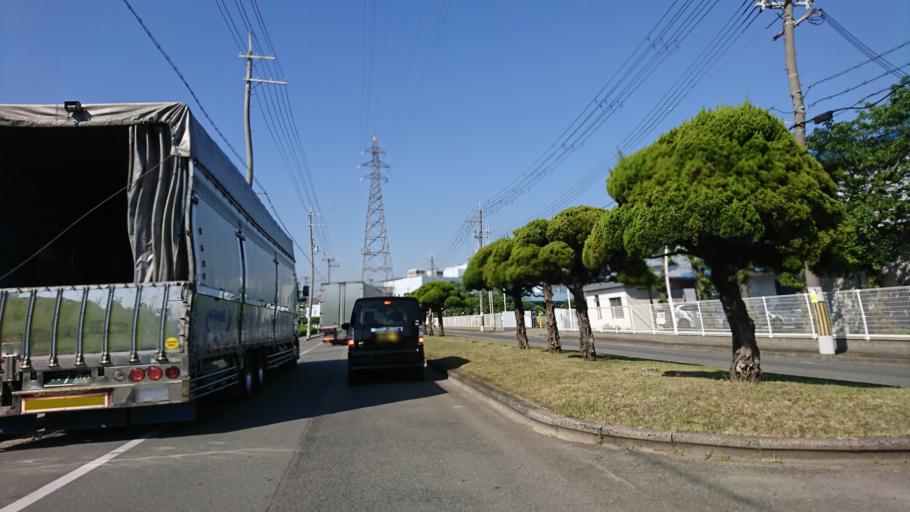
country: JP
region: Hyogo
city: Kakogawacho-honmachi
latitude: 34.7619
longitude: 134.8671
